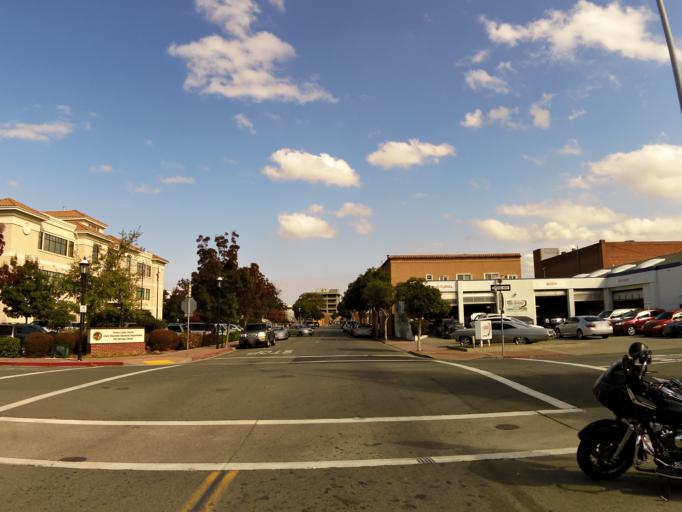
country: US
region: California
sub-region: Contra Costa County
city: Martinez
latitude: 38.0169
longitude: -122.1389
